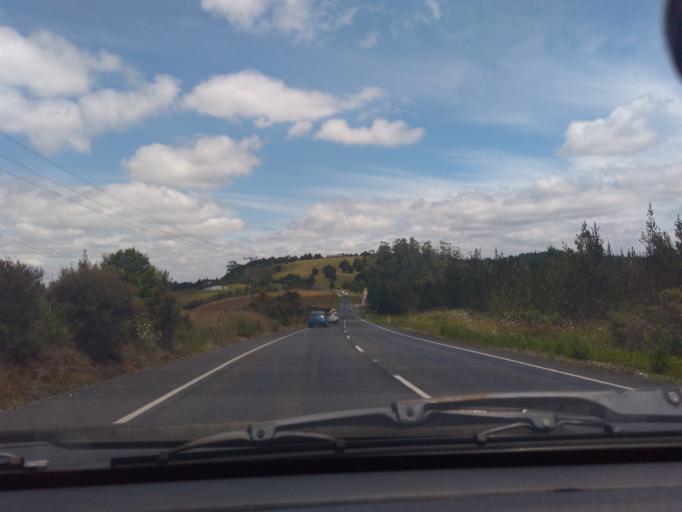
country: NZ
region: Northland
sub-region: Far North District
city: Kerikeri
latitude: -35.1401
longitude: 173.8828
